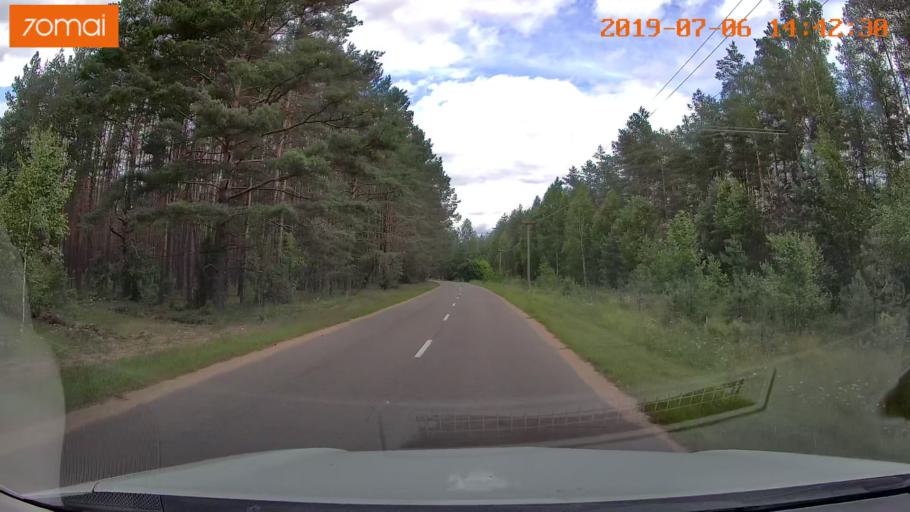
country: BY
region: Minsk
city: Ivyanyets
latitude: 53.9419
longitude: 26.6897
